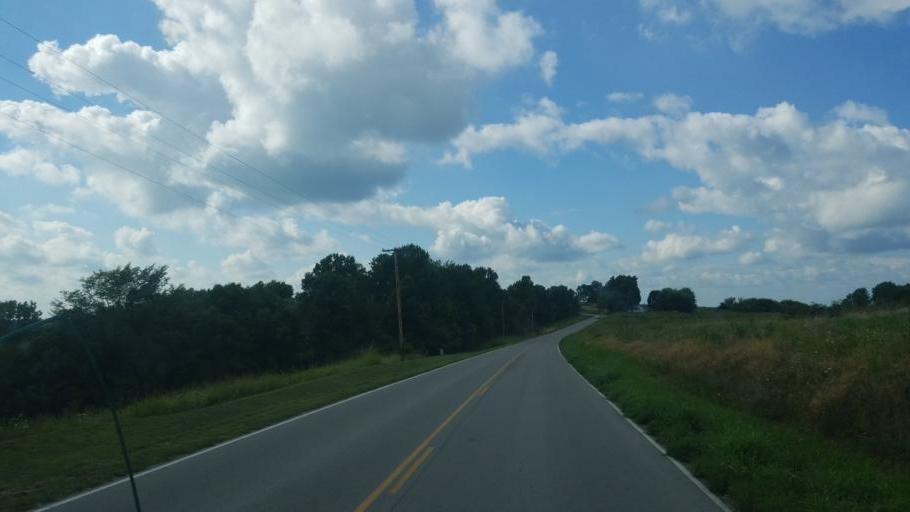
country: US
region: Illinois
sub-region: Union County
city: Cobden
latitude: 37.5503
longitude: -89.2953
